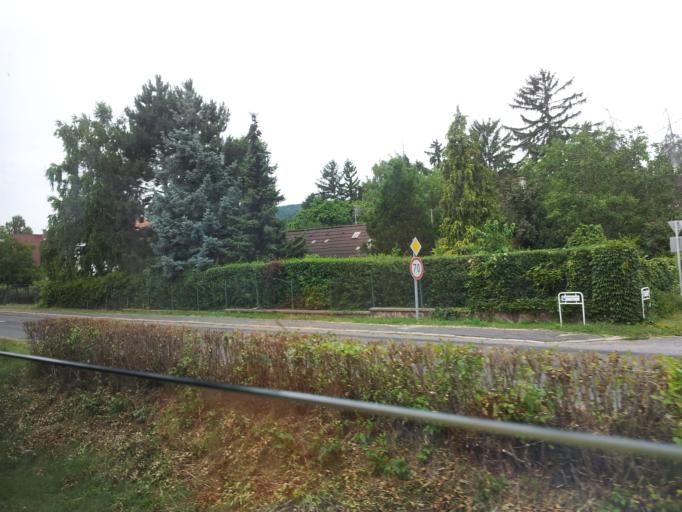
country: HU
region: Veszprem
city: Zanka
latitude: 46.8493
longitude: 17.6604
